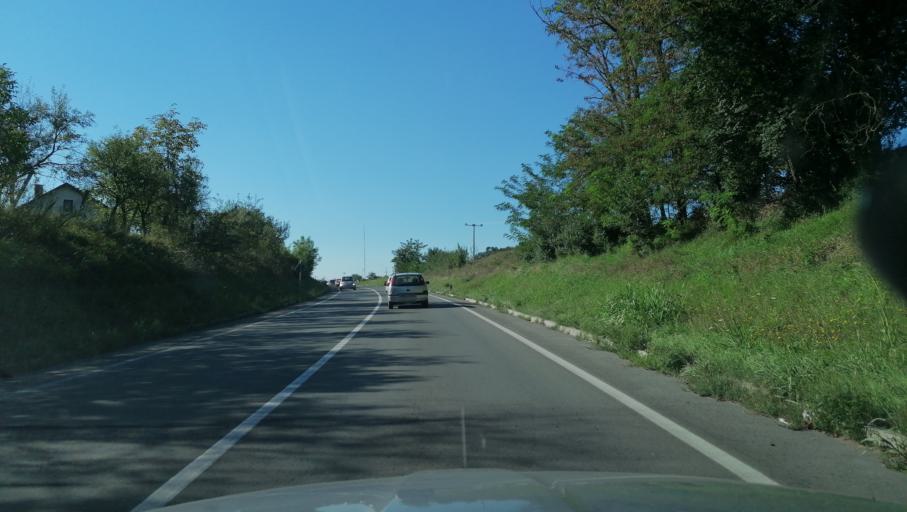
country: RS
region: Central Serbia
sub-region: Raski Okrug
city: Kraljevo
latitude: 43.8174
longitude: 20.6115
